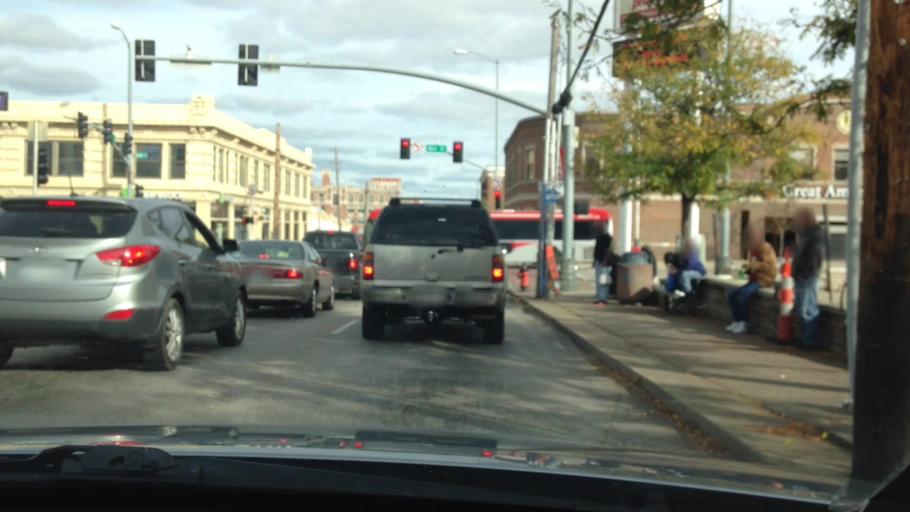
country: US
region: Kansas
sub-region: Johnson County
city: Westwood
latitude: 39.0566
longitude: -94.5867
